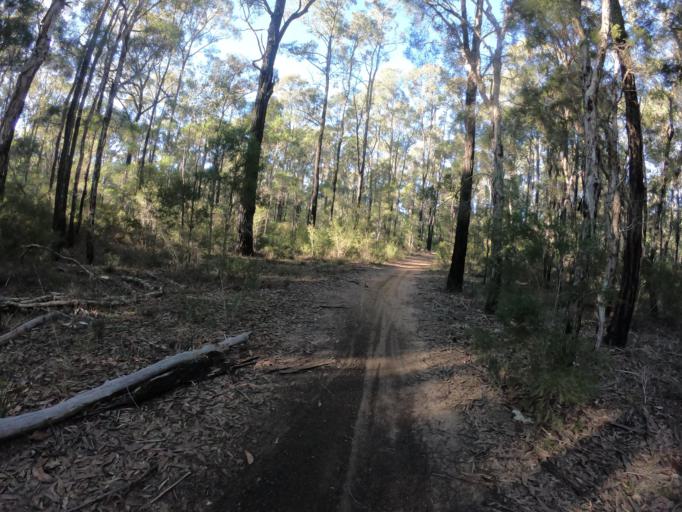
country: AU
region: New South Wales
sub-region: Hawkesbury
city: South Windsor
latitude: -33.6437
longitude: 150.7964
